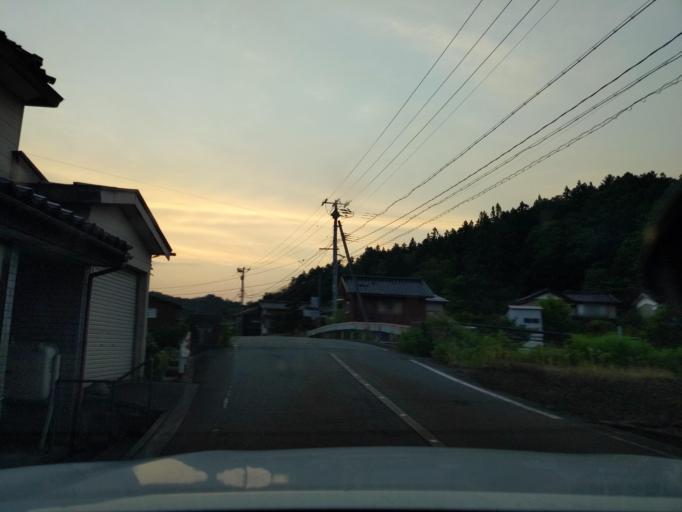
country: JP
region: Niigata
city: Kashiwazaki
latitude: 37.4488
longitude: 138.6399
